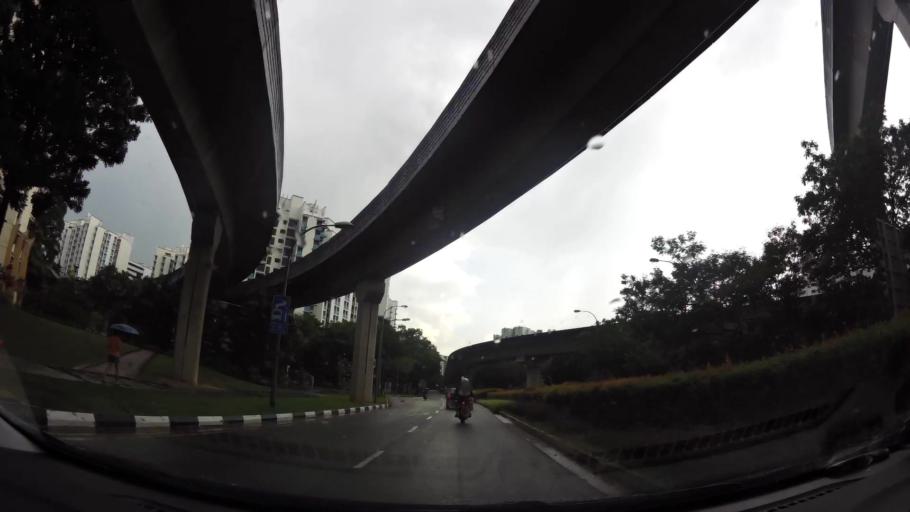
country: MY
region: Johor
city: Kampung Pasir Gudang Baru
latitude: 1.3956
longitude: 103.8966
